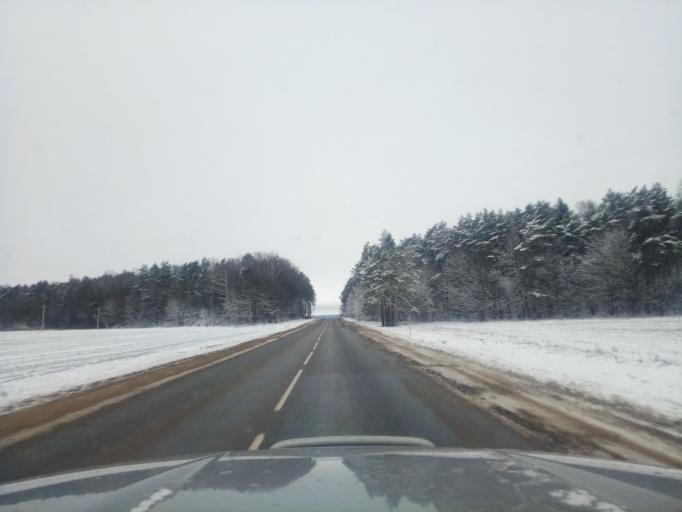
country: BY
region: Minsk
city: Kapyl'
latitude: 53.1560
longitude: 27.1107
